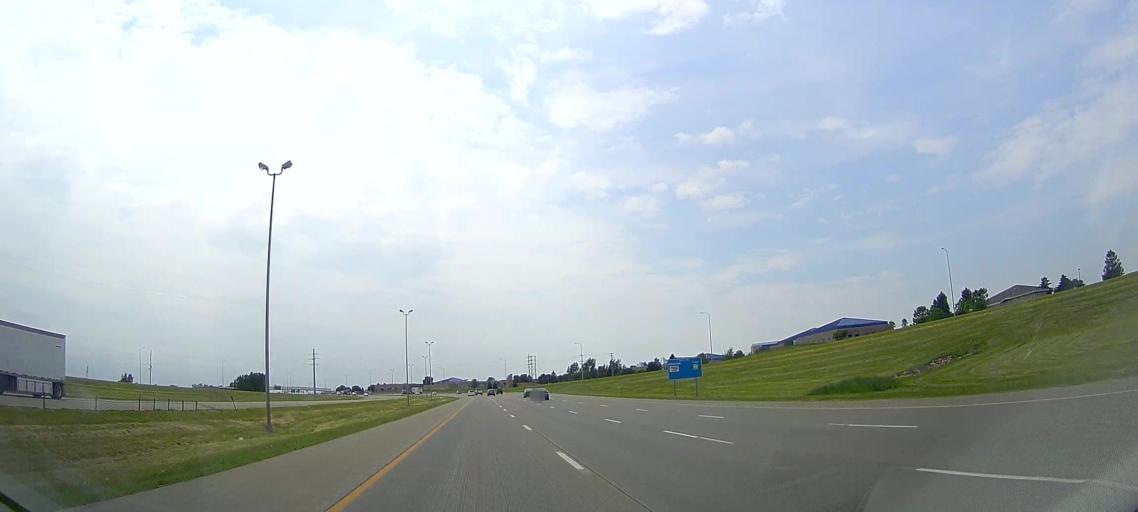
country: US
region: South Dakota
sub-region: Minnehaha County
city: Sioux Falls
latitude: 43.5718
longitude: -96.7761
